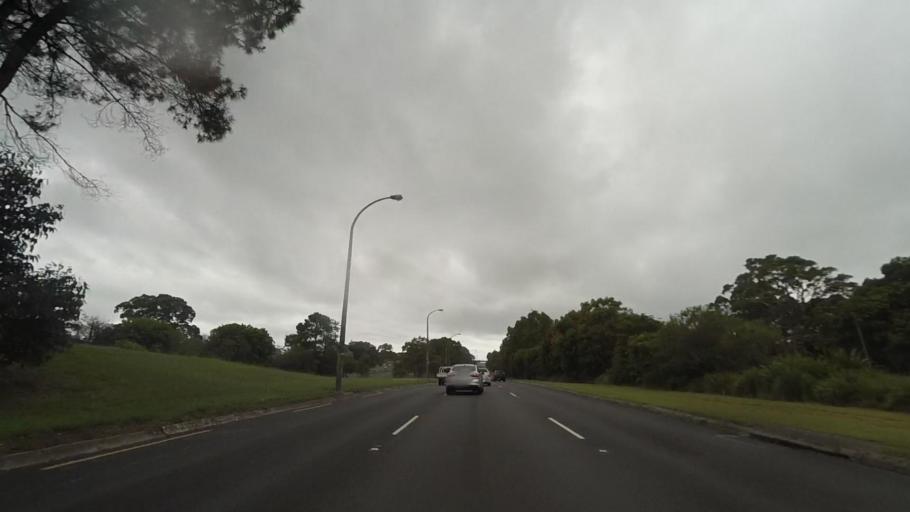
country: AU
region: New South Wales
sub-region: Kogarah
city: Blakehurst
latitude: -34.0170
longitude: 151.1224
